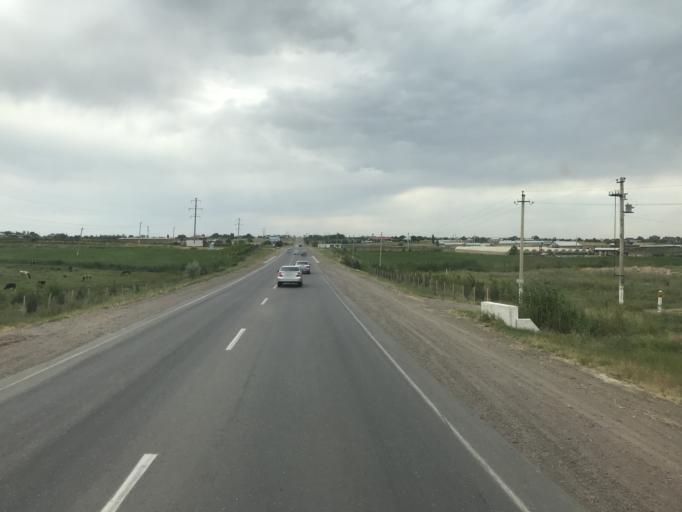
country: KZ
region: Ongtustik Qazaqstan
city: Saryaghash
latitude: 41.4538
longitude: 69.1357
